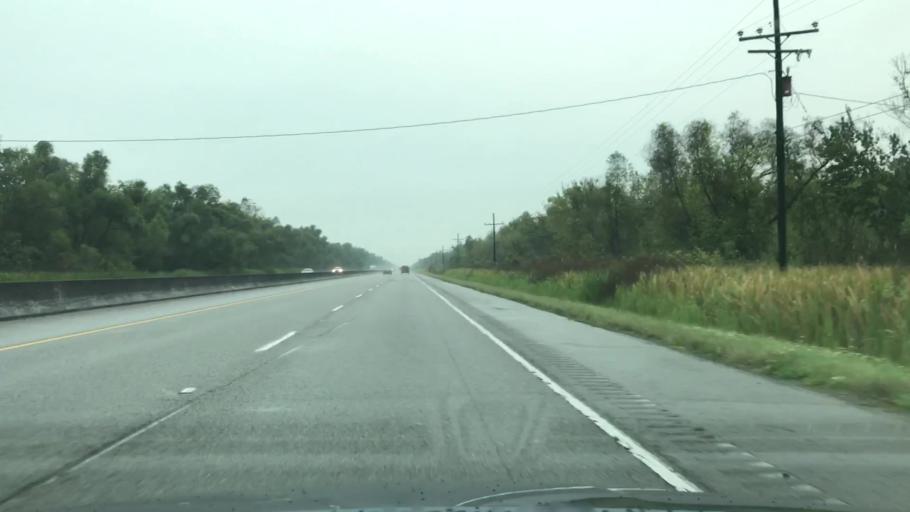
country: US
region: Louisiana
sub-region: Saint Charles Parish
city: Des Allemands
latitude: 29.7820
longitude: -90.5241
